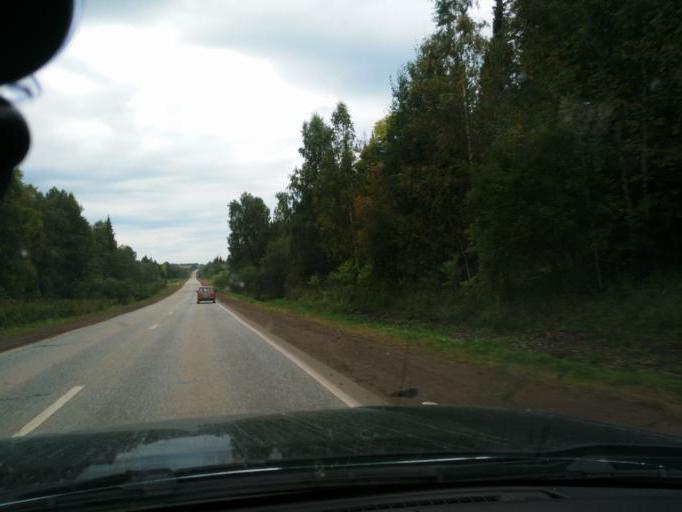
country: RU
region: Perm
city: Chernushka
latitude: 56.8029
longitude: 56.0658
